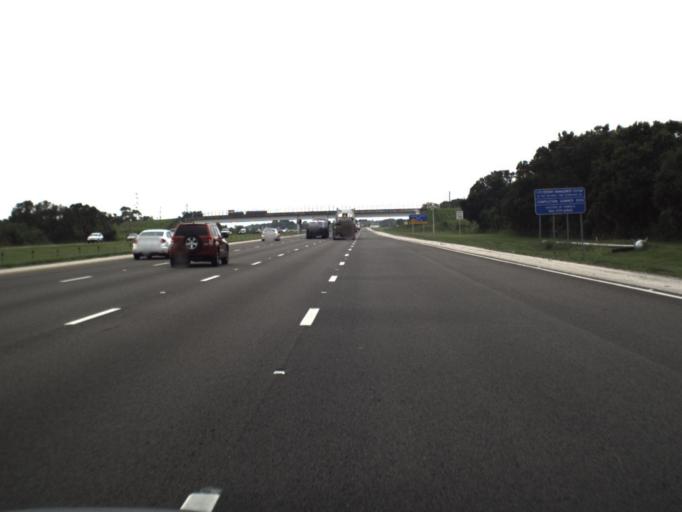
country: US
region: Florida
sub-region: Manatee County
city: Ellenton
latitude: 27.5780
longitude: -82.5149
